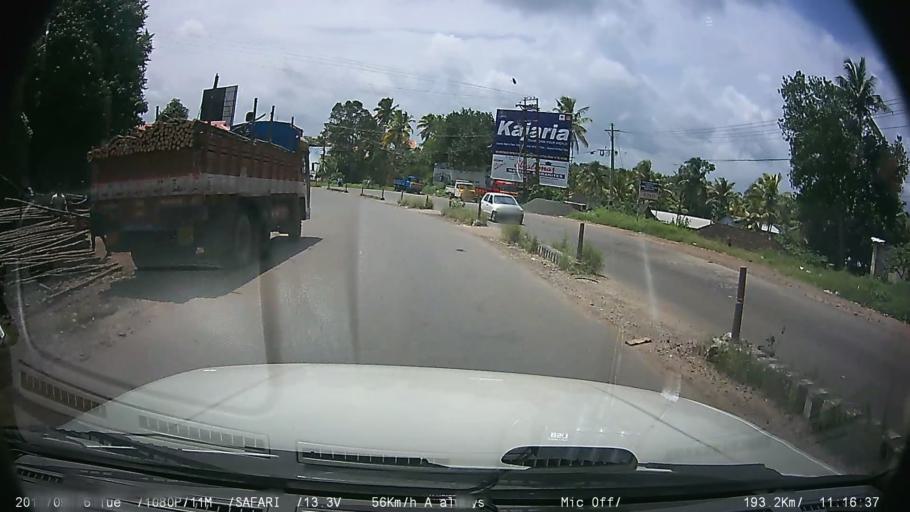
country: IN
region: Kerala
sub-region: Kottayam
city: Changanacheri
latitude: 9.5024
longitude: 76.5244
